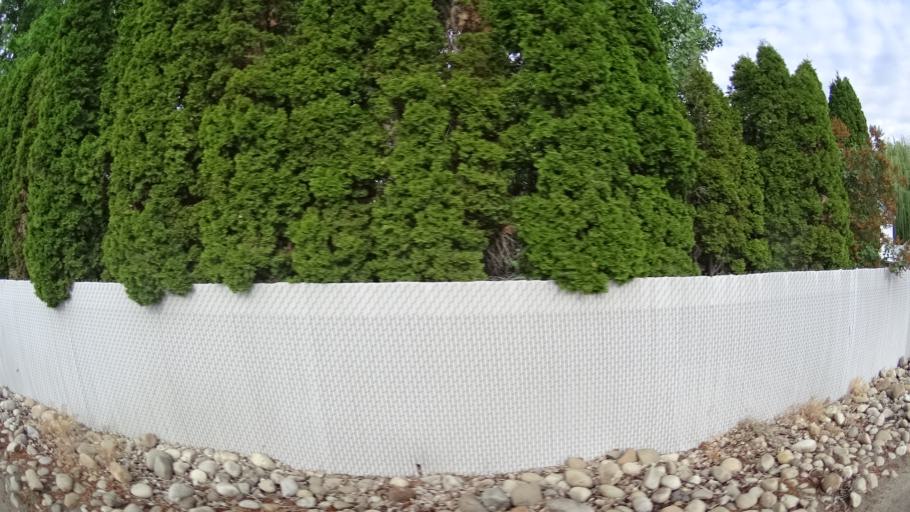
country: US
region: Idaho
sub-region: Ada County
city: Star
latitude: 43.7130
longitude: -116.5126
